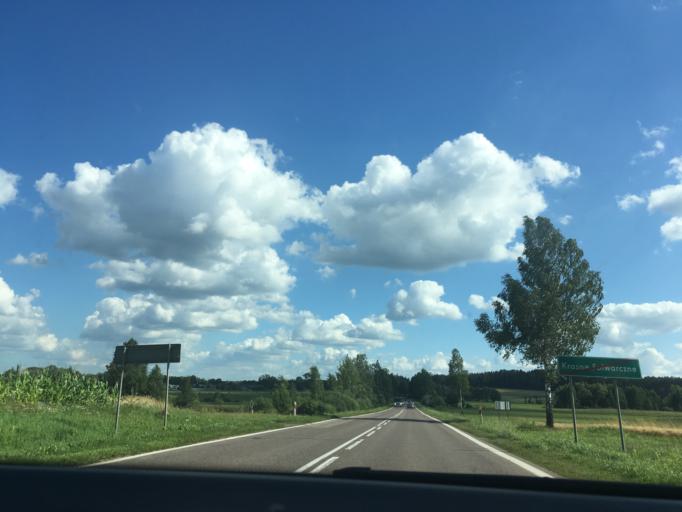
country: PL
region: Podlasie
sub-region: Powiat bialostocki
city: Dobrzyniewo Duze
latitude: 53.3439
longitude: 23.0995
